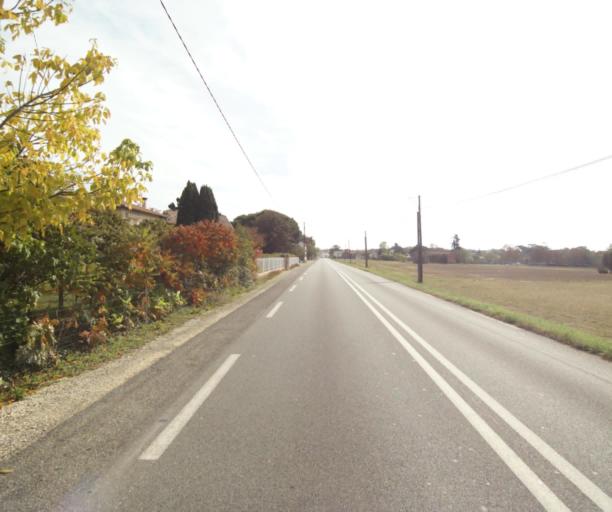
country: FR
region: Midi-Pyrenees
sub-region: Departement du Tarn-et-Garonne
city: Orgueil
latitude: 43.9208
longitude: 1.3953
